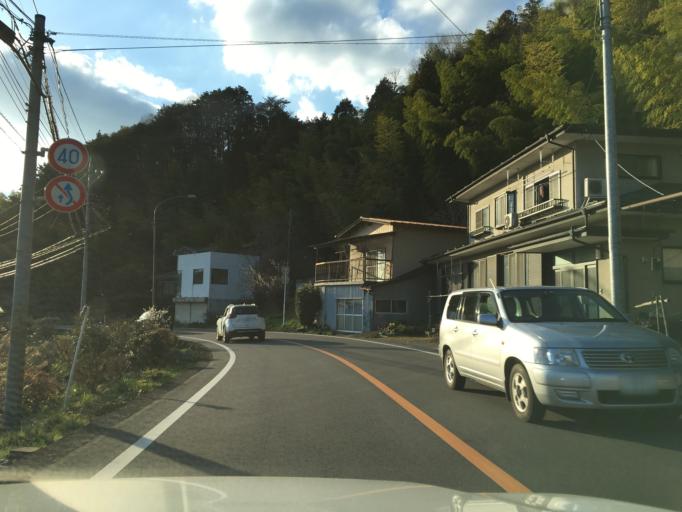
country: JP
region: Tochigi
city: Otawara
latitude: 36.8705
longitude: 140.1489
